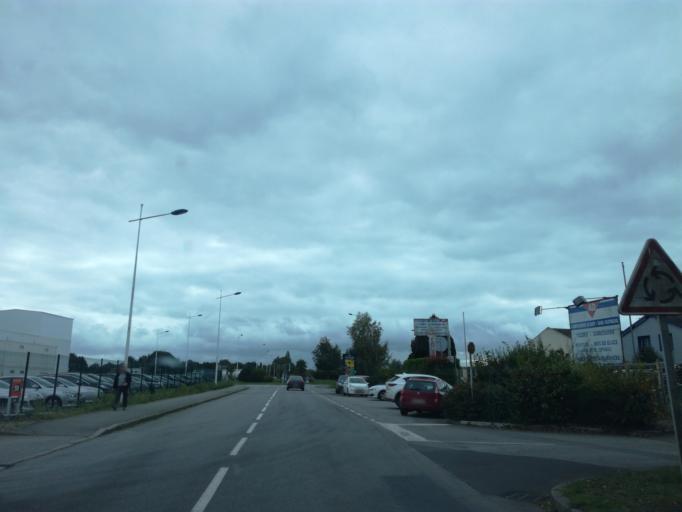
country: FR
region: Brittany
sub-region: Departement des Cotes-d'Armor
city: Loudeac
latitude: 48.1616
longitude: -2.7544
